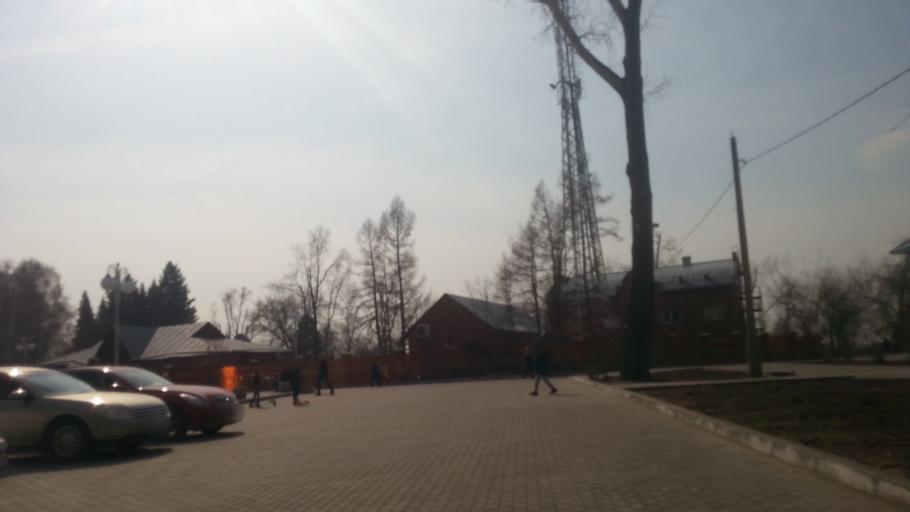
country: RU
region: Altai Krai
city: Zaton
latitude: 53.3232
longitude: 83.7957
